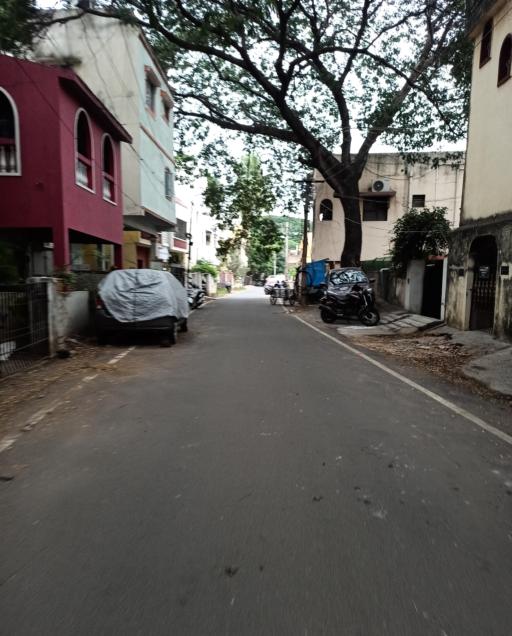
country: IN
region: Tamil Nadu
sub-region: Thiruvallur
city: Porur
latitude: 13.0553
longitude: 80.1957
